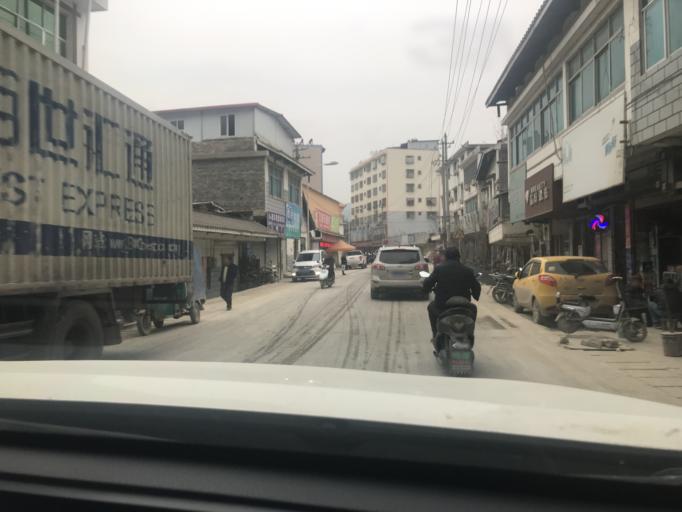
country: CN
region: Guangxi Zhuangzu Zizhiqu
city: Xinzhou
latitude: 24.9831
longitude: 105.8080
